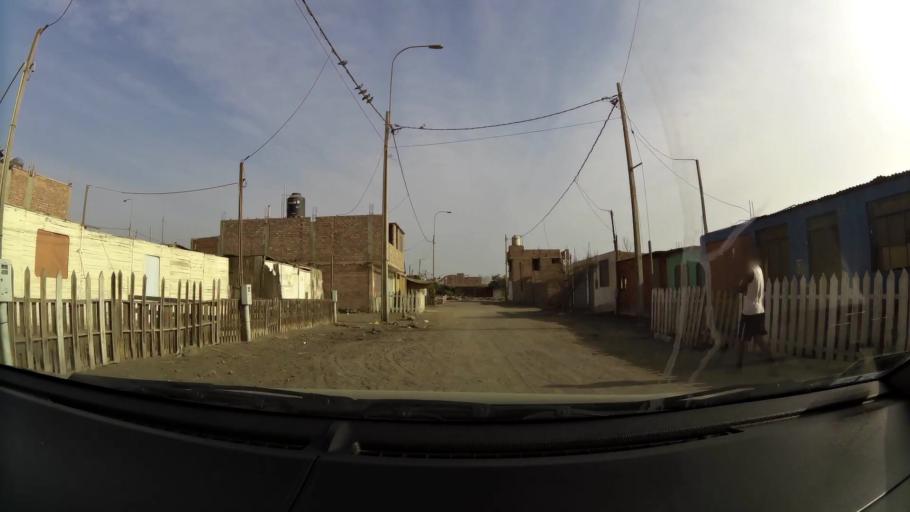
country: PE
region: Lima
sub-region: Lima
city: Santa Rosa
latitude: -11.7603
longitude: -77.1684
